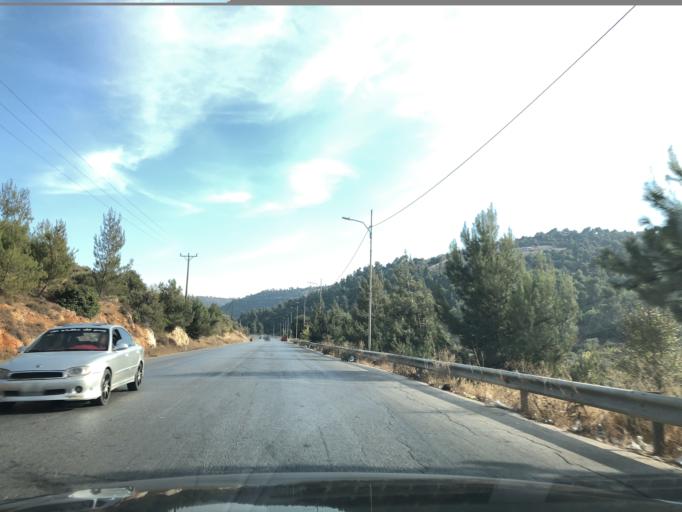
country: JO
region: Irbid
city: Sakib
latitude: 32.2916
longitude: 35.7909
